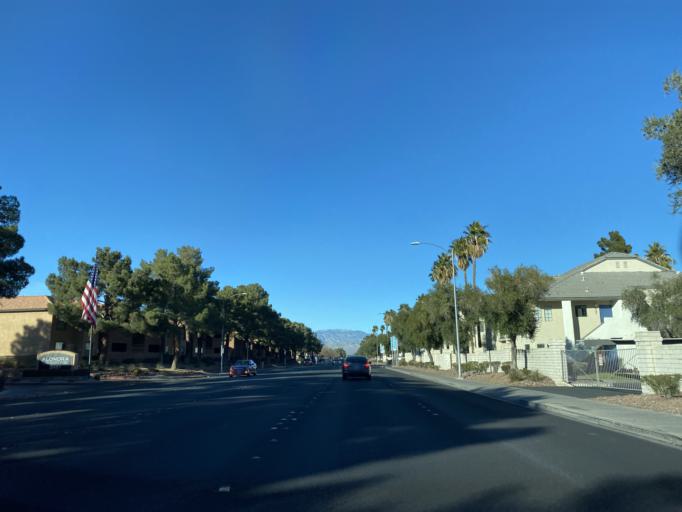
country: US
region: Nevada
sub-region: Clark County
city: Spring Valley
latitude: 36.2048
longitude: -115.2422
